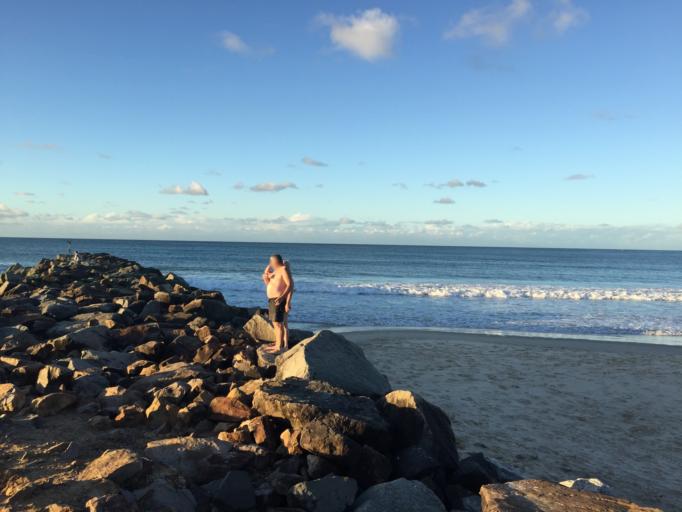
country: AU
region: Queensland
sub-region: Sunshine Coast
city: Noosa Heads
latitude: -26.3844
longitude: 153.0866
